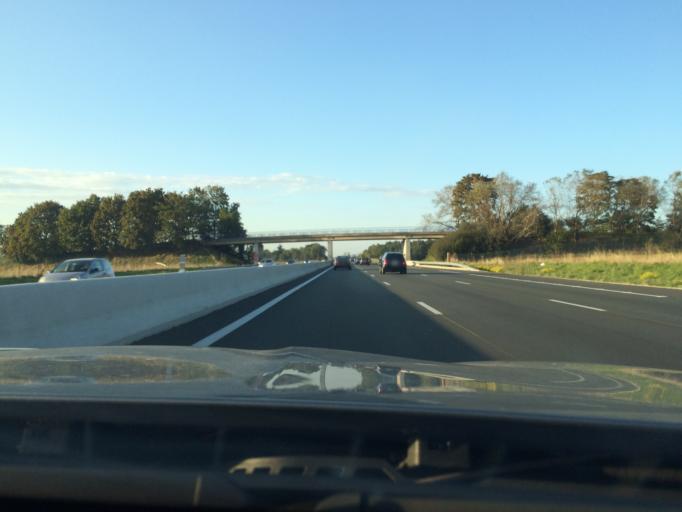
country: FR
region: Ile-de-France
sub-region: Departement de l'Essonne
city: Le Coudray-Montceaux
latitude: 48.5418
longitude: 2.4979
